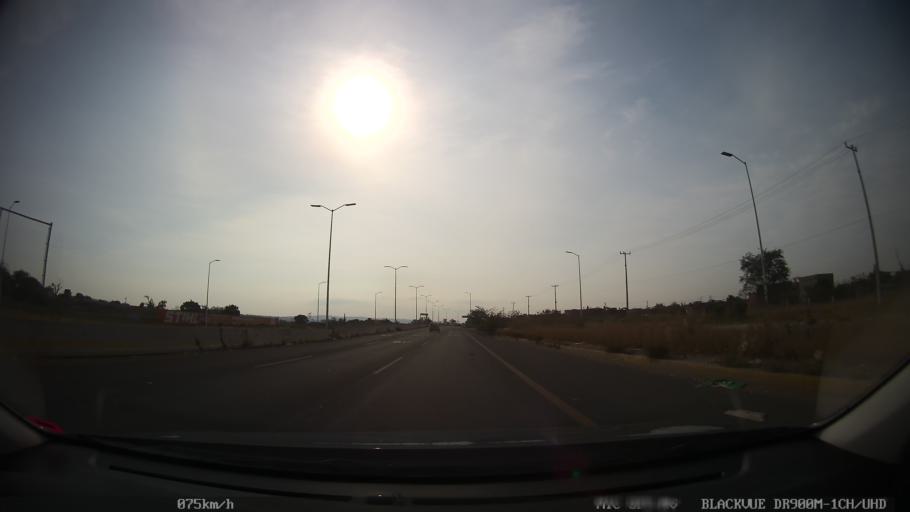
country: MX
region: Jalisco
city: Tonala
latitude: 20.6836
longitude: -103.2418
